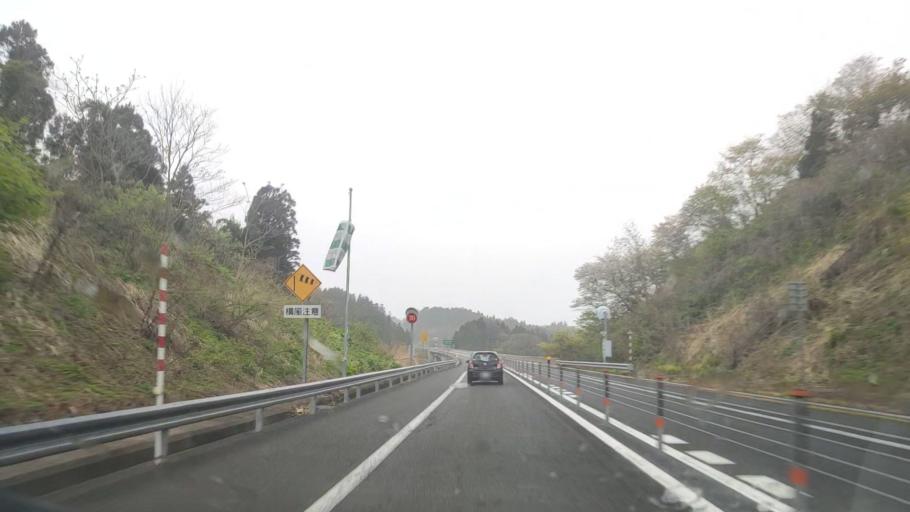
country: JP
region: Akita
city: Noshiromachi
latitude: 40.2004
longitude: 140.1351
